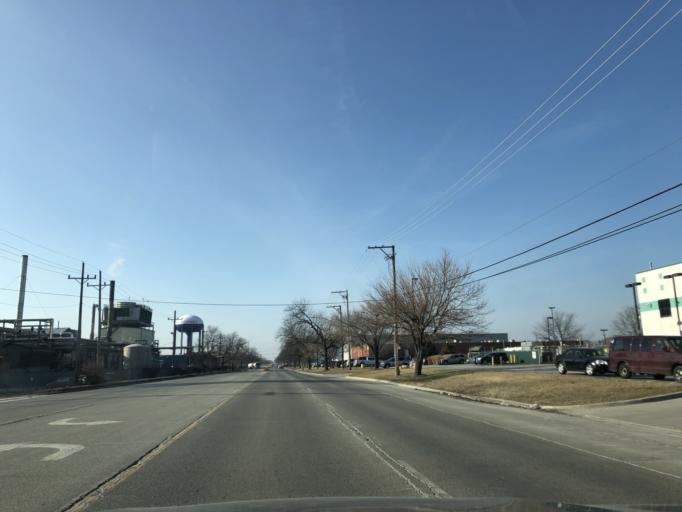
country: US
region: Illinois
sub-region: Cook County
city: Cicero
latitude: 41.8220
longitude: -87.7480
